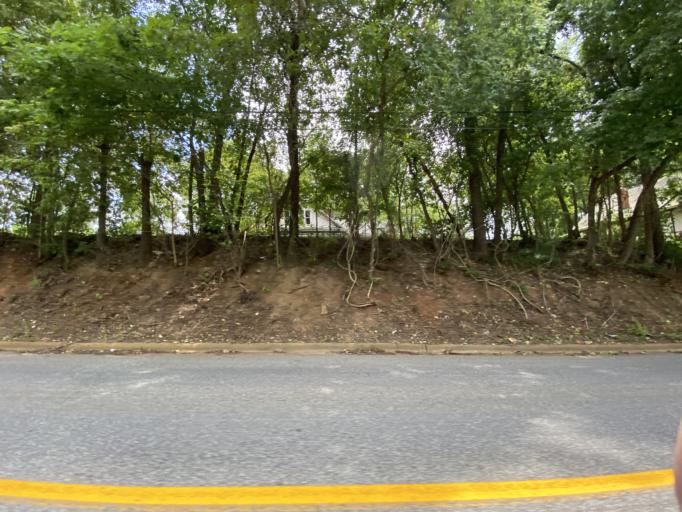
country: US
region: Missouri
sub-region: Oregon County
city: Thayer
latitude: 36.4957
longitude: -91.5471
